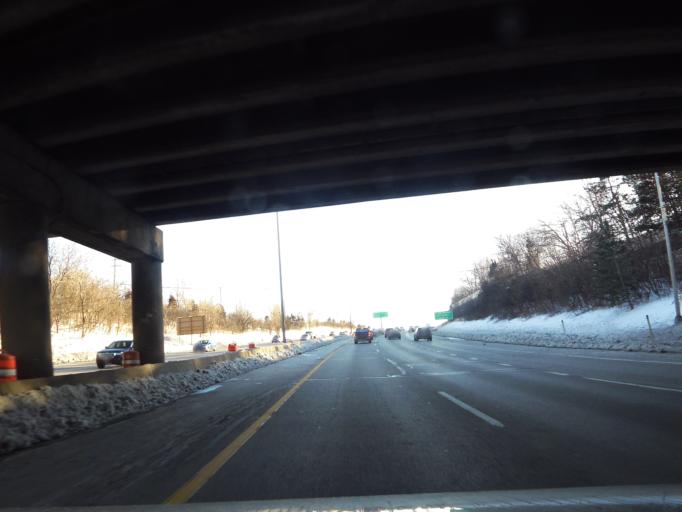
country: US
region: Wisconsin
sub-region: Milwaukee County
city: Greenfield
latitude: 42.9739
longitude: -88.0385
